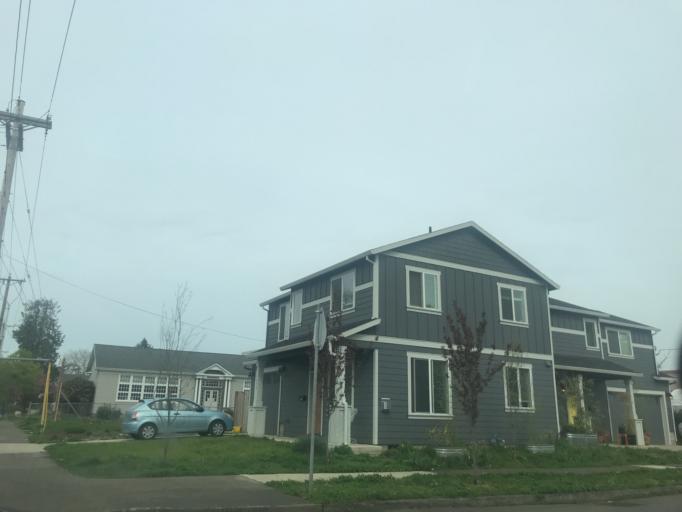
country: US
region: Oregon
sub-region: Multnomah County
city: Lents
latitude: 45.4866
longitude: -122.5820
